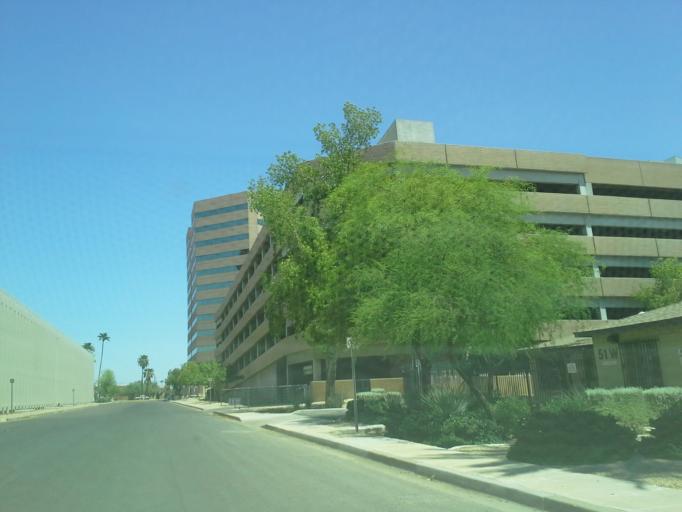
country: US
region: Arizona
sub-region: Maricopa County
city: Phoenix
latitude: 33.4908
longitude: -112.0764
